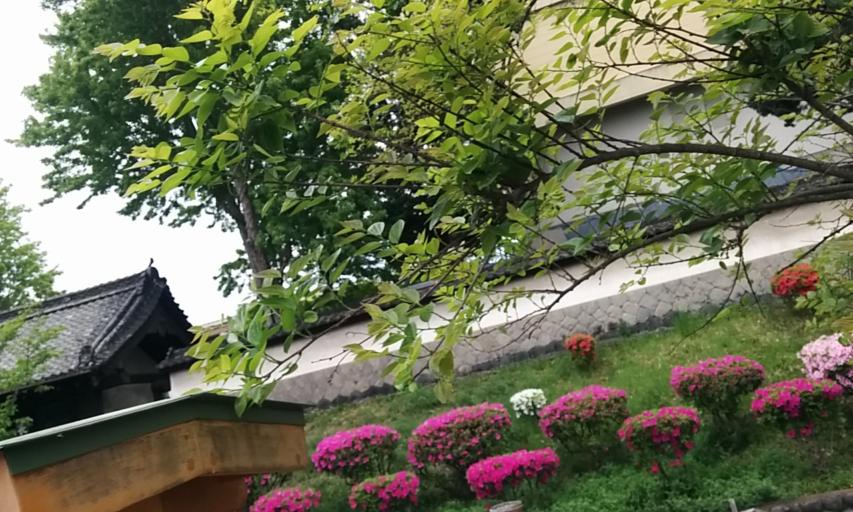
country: JP
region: Nagano
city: Ueda
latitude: 36.4007
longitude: 138.2499
